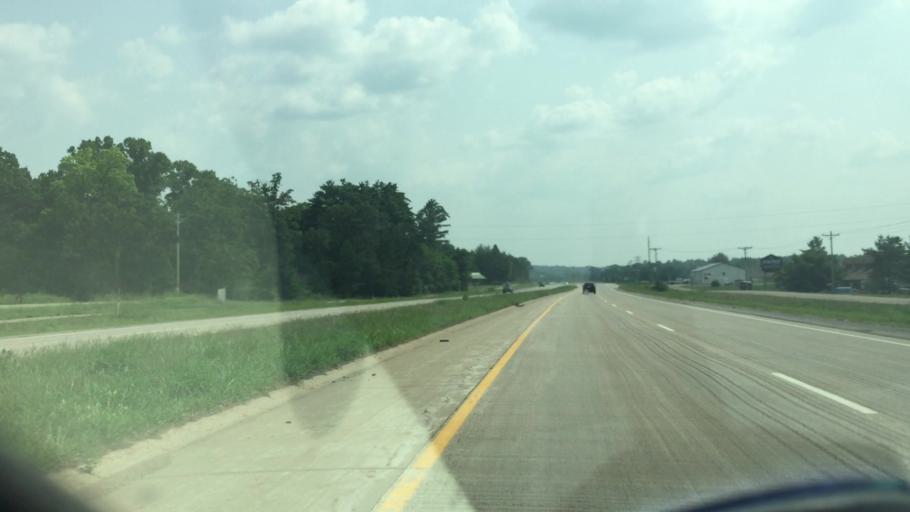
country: US
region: Wisconsin
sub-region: Eau Claire County
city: Altoona
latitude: 44.7501
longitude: -91.4530
